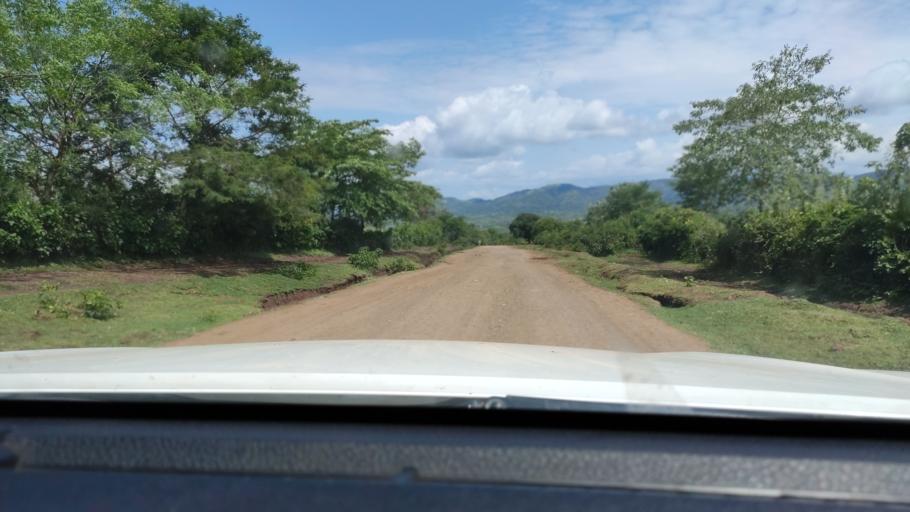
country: ET
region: Southern Nations, Nationalities, and People's Region
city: Felege Neway
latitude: 6.3653
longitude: 36.9862
